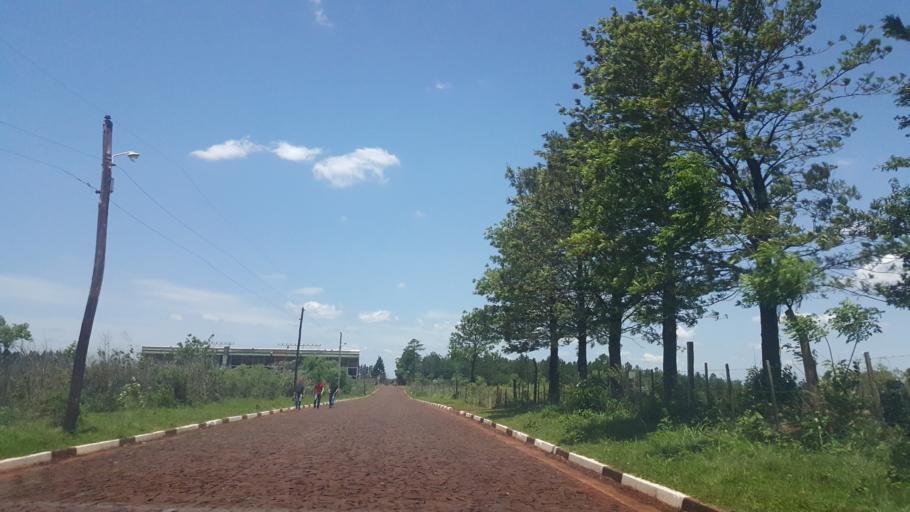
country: AR
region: Misiones
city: Garupa
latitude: -27.4969
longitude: -55.8560
